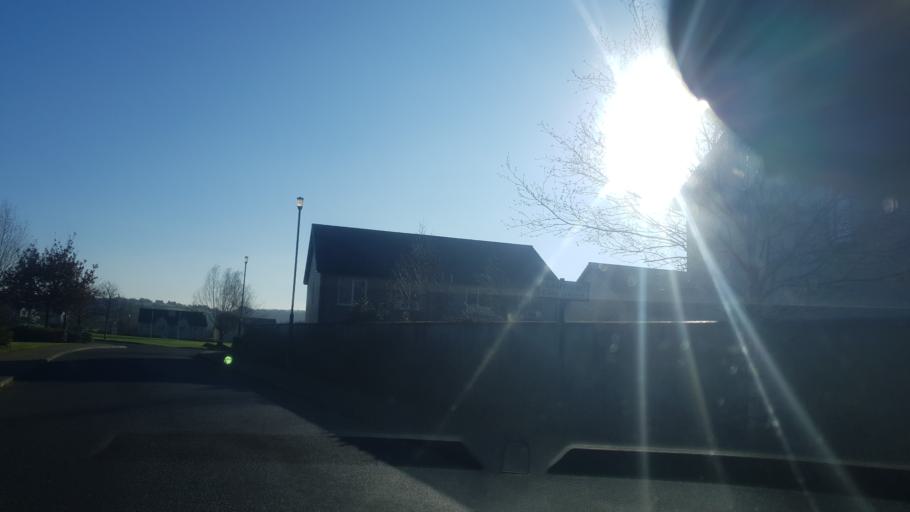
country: IE
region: Munster
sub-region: Ciarrai
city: Cill Airne
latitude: 52.0943
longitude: -9.4761
